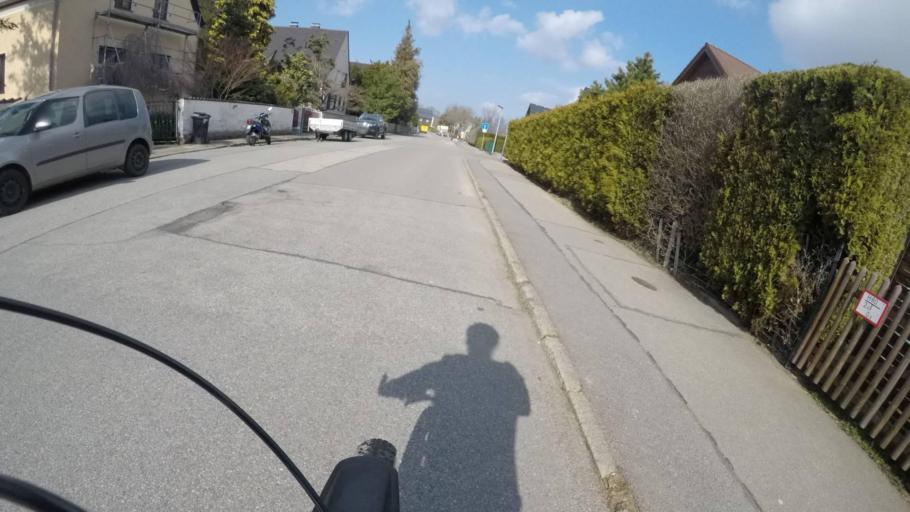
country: DE
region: Saxony
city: Limbach-Oberfrohna
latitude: 50.8530
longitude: 12.7586
